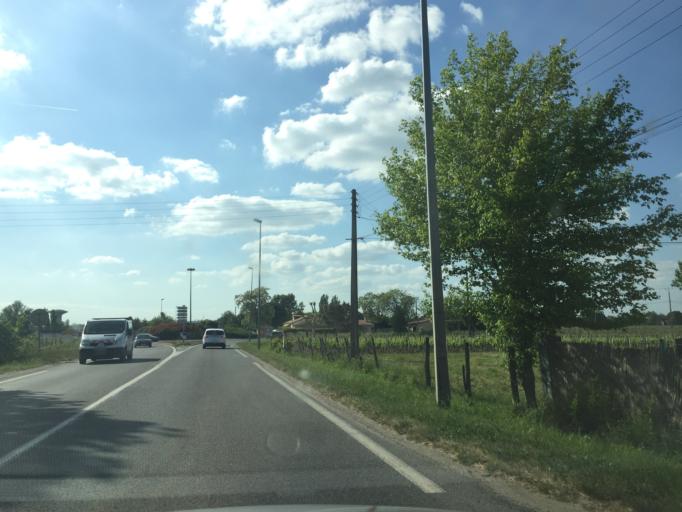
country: FR
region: Aquitaine
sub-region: Departement de la Gironde
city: Libourne
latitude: 44.8959
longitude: -0.2049
